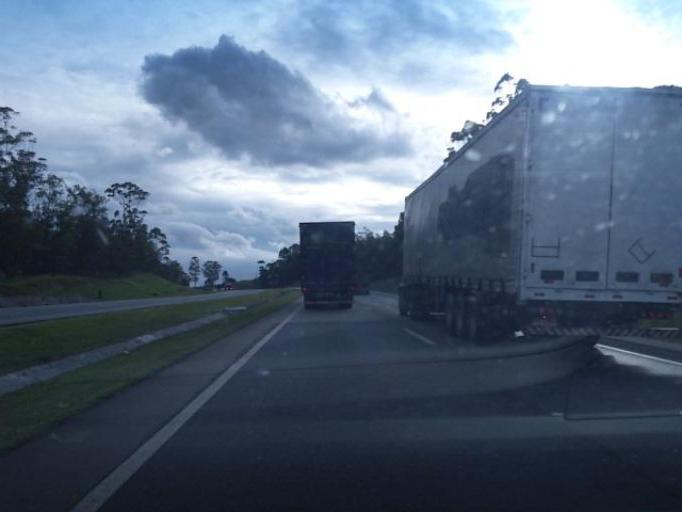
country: BR
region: Parana
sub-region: Piraquara
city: Piraquara
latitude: -25.4331
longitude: -49.0873
